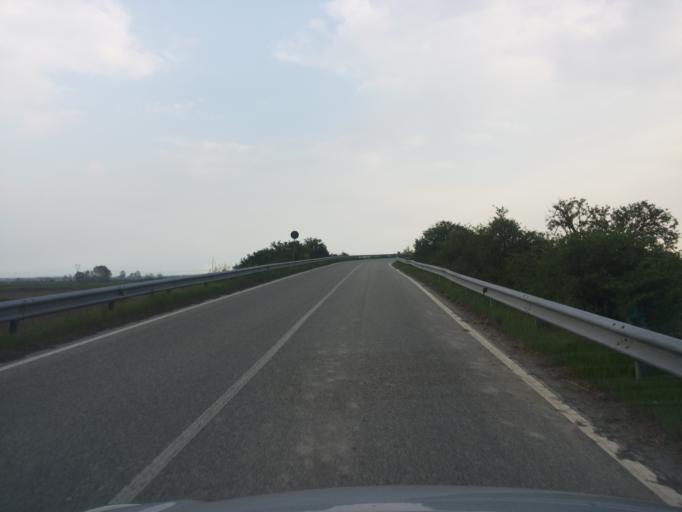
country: IT
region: Piedmont
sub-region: Provincia di Alessandria
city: Villanova Monferrato
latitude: 45.1935
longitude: 8.4950
